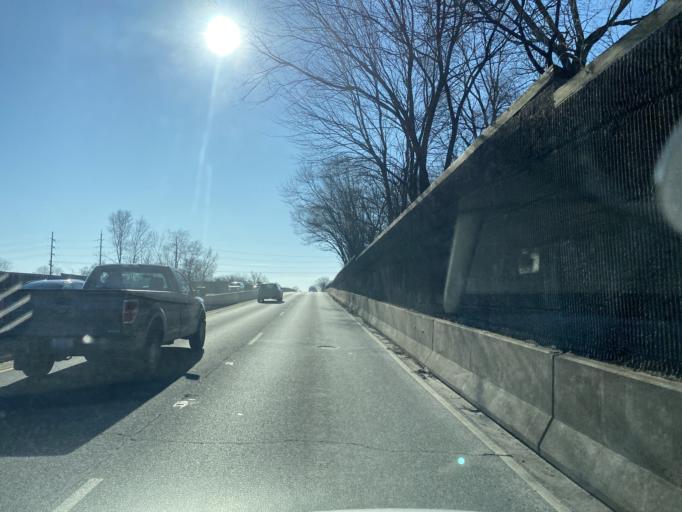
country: US
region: Illinois
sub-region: DuPage County
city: Clarendon Hills
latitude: 41.8002
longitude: -87.9465
